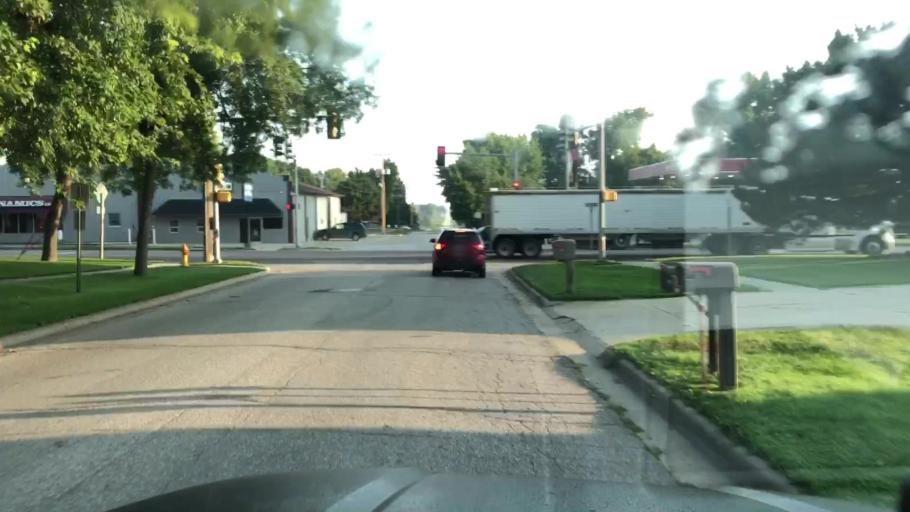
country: US
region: Iowa
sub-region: O'Brien County
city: Sheldon
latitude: 43.1846
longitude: -95.8422
